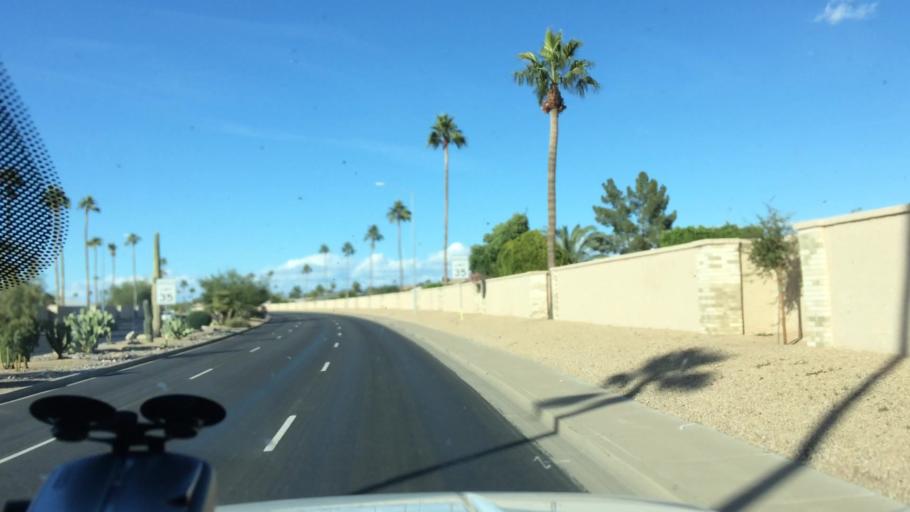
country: US
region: Arizona
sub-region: Maricopa County
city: Surprise
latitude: 33.6436
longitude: -112.3344
